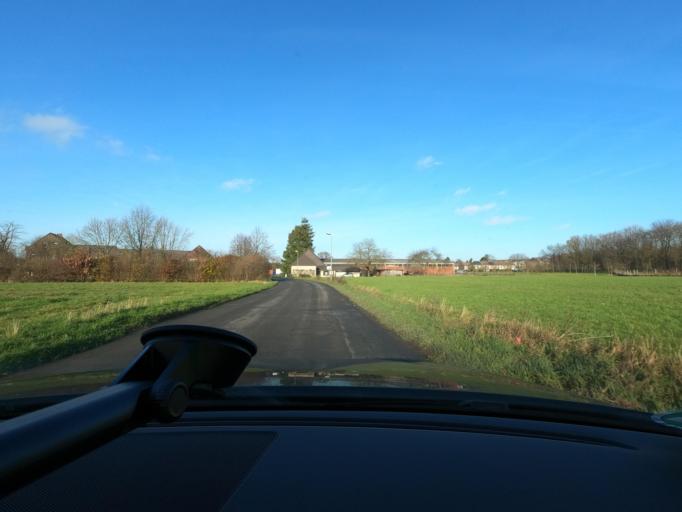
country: DE
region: North Rhine-Westphalia
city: Tonisvorst
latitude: 51.3441
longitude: 6.5201
